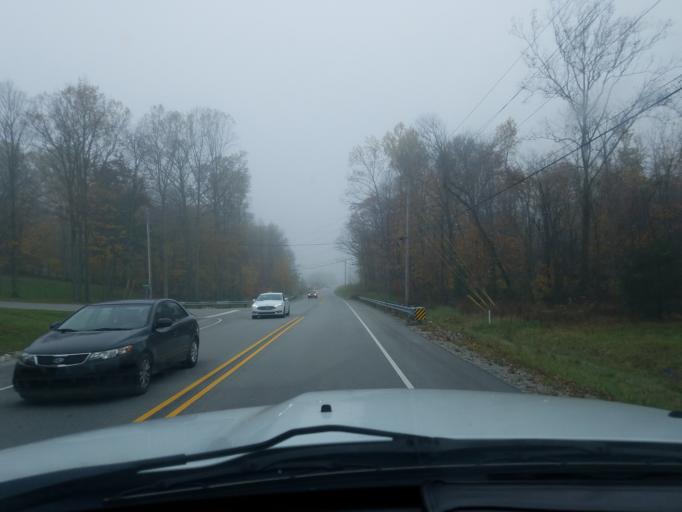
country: US
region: Indiana
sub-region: Floyd County
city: Galena
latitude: 38.3271
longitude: -85.9181
